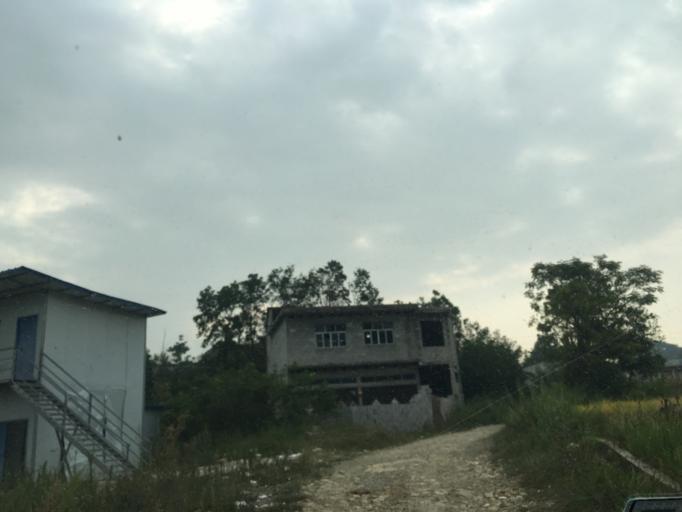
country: CN
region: Guangxi Zhuangzu Zizhiqu
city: Xinzhou
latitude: 25.4451
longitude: 105.6479
